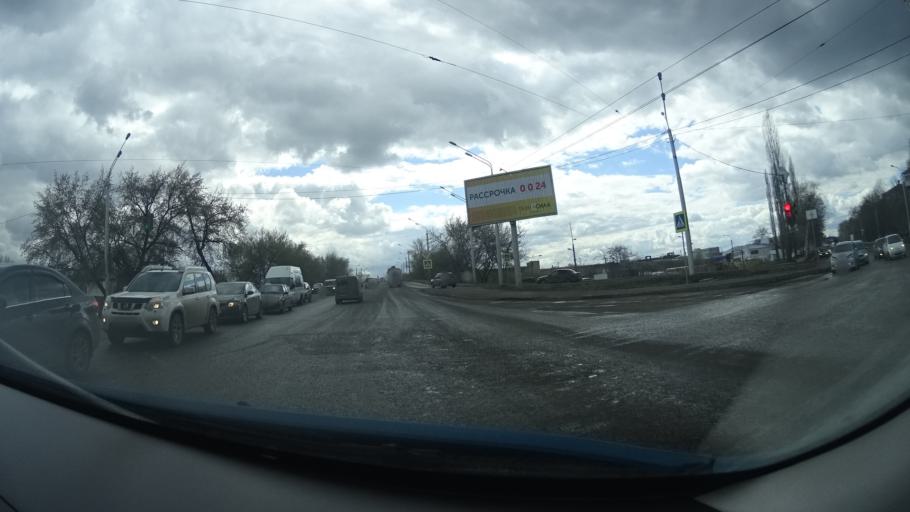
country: RU
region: Bashkortostan
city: Ufa
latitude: 54.8107
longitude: 56.0873
